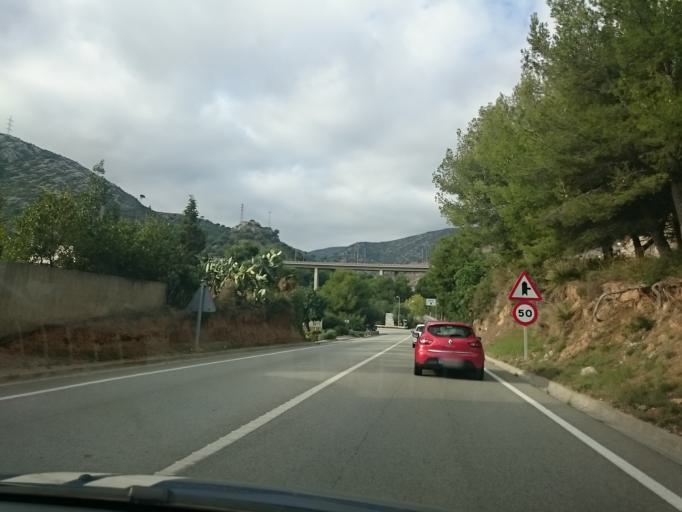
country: ES
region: Catalonia
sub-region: Provincia de Barcelona
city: Castelldefels
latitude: 41.2564
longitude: 1.9055
